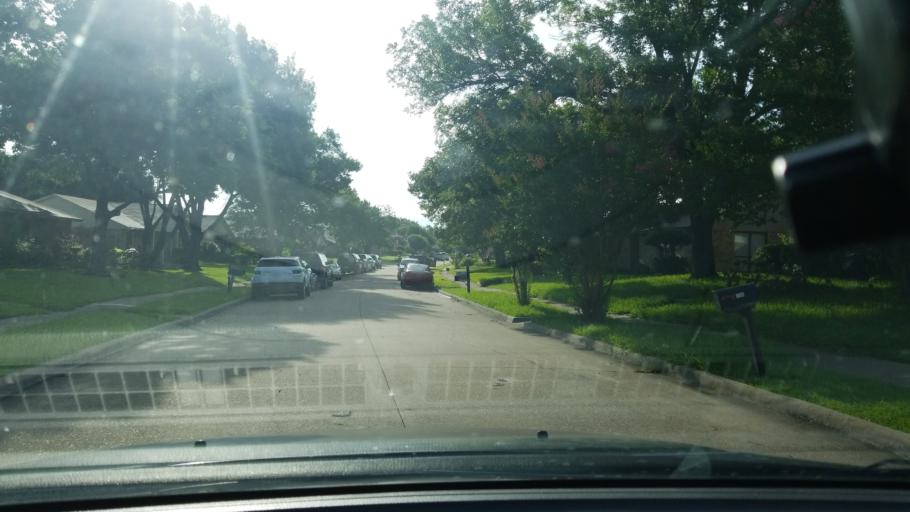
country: US
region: Texas
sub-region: Dallas County
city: Mesquite
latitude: 32.8108
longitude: -96.6077
